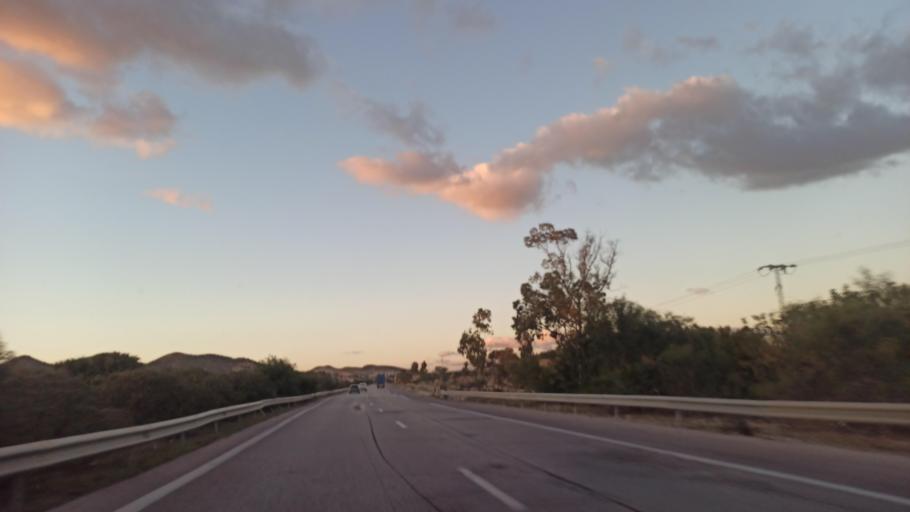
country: TN
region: Susah
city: Harqalah
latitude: 36.2174
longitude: 10.4196
